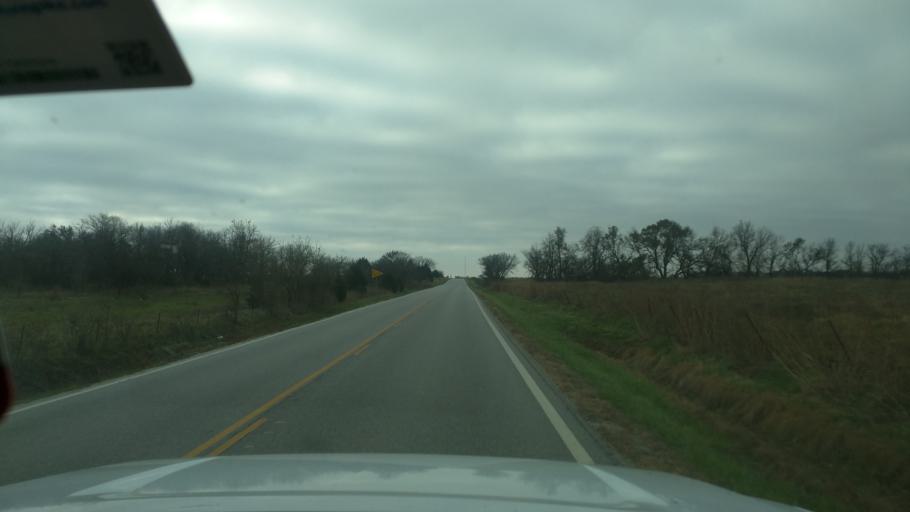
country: US
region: Kansas
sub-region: Greenwood County
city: Eureka
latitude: 37.6587
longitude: -96.2345
